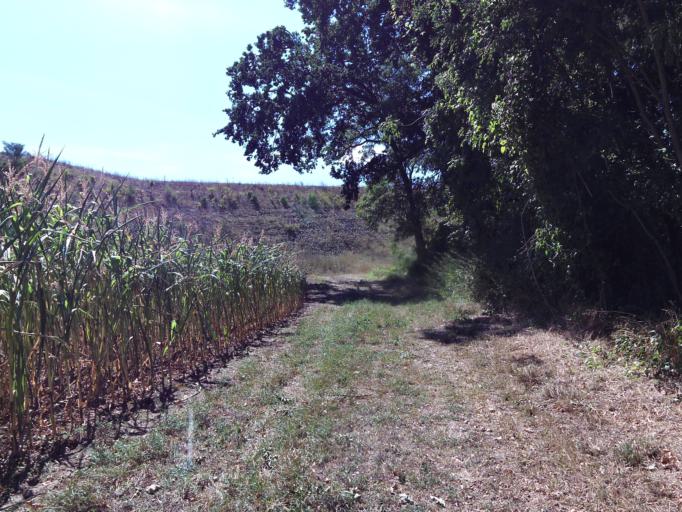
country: DE
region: Bavaria
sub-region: Regierungsbezirk Unterfranken
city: Theilheim
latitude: 49.7510
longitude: 10.0386
